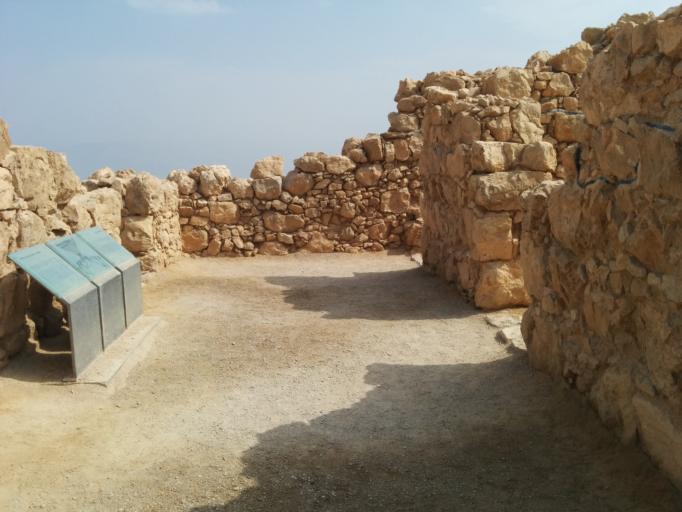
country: IL
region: Southern District
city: `En Boqeq
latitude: 31.3176
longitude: 35.3543
